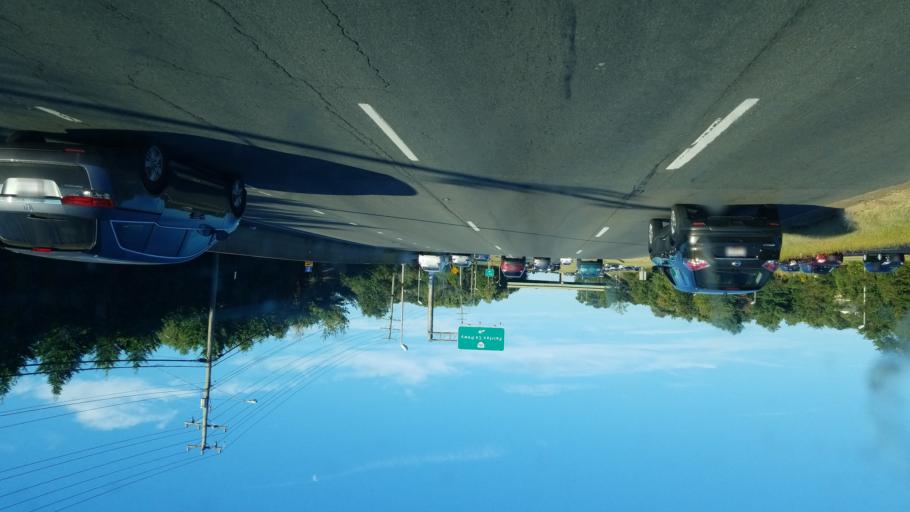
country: US
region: Virginia
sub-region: Fairfax County
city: Greenbriar
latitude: 38.8772
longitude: -77.3879
